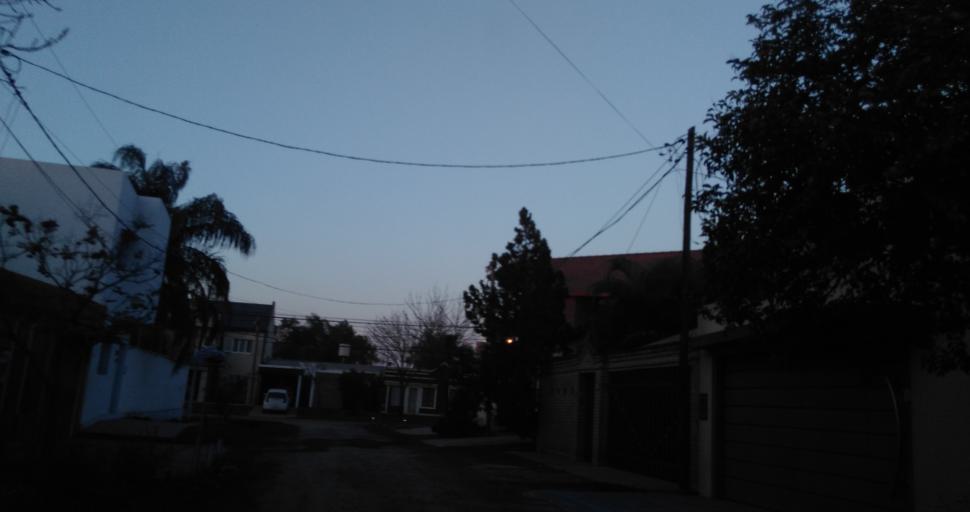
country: AR
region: Chaco
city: Resistencia
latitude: -27.4384
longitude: -58.9696
